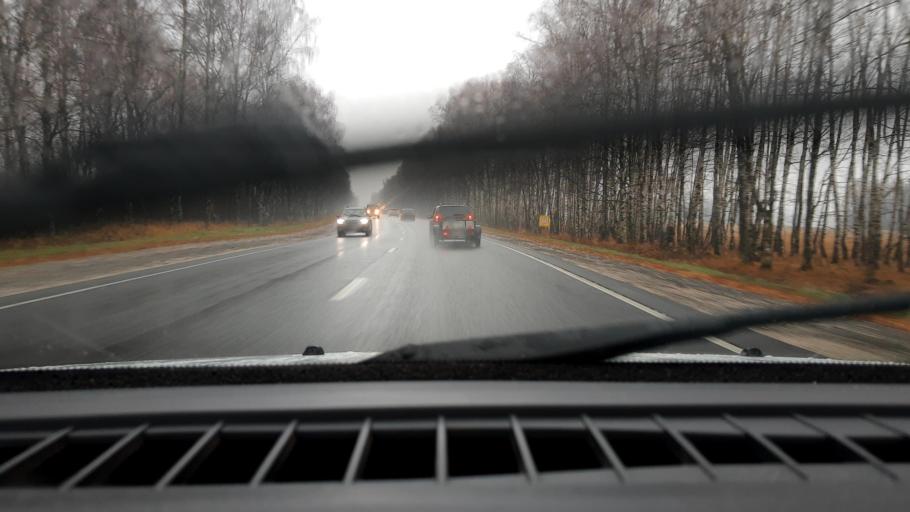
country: RU
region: Nizjnij Novgorod
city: Sitniki
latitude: 56.5378
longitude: 44.0208
